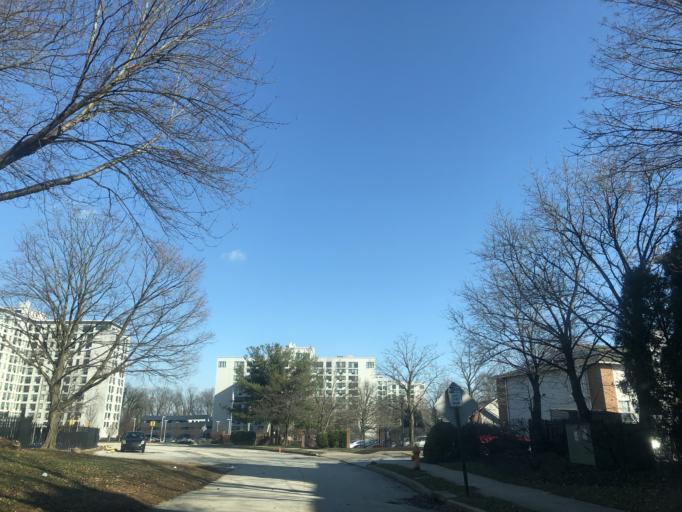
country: US
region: Pennsylvania
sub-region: Montgomery County
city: Bala-Cynwyd
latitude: 40.0021
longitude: -75.2136
